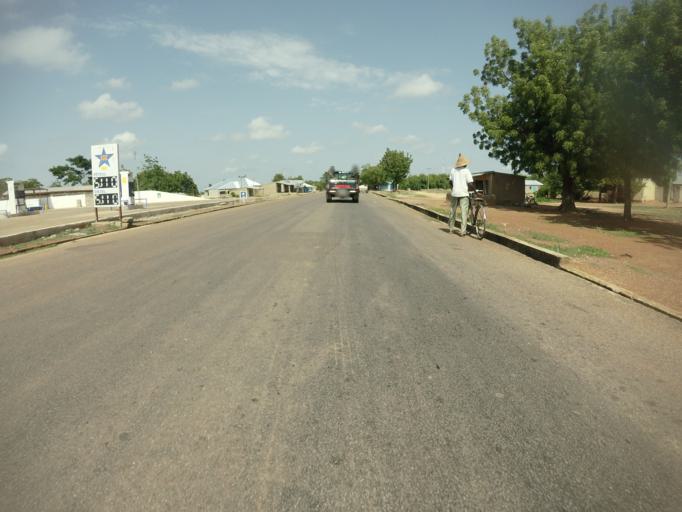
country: GH
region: Upper East
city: Bawku
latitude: 11.0700
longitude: -0.2040
